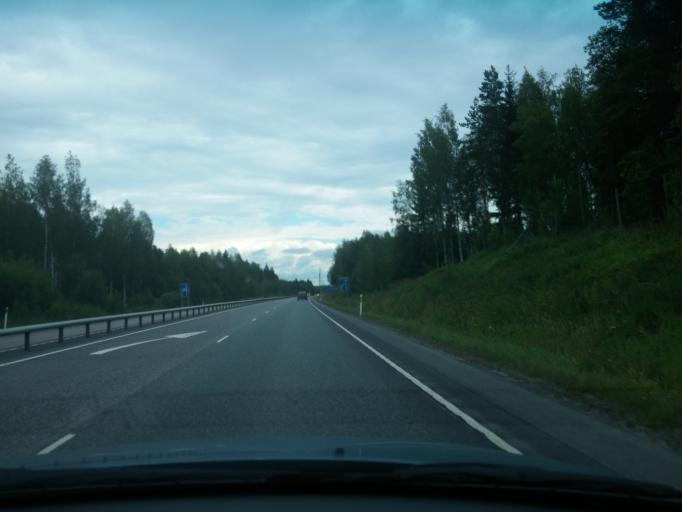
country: FI
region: Haeme
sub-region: Riihimaeki
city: Loppi
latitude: 60.7235
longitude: 24.5061
